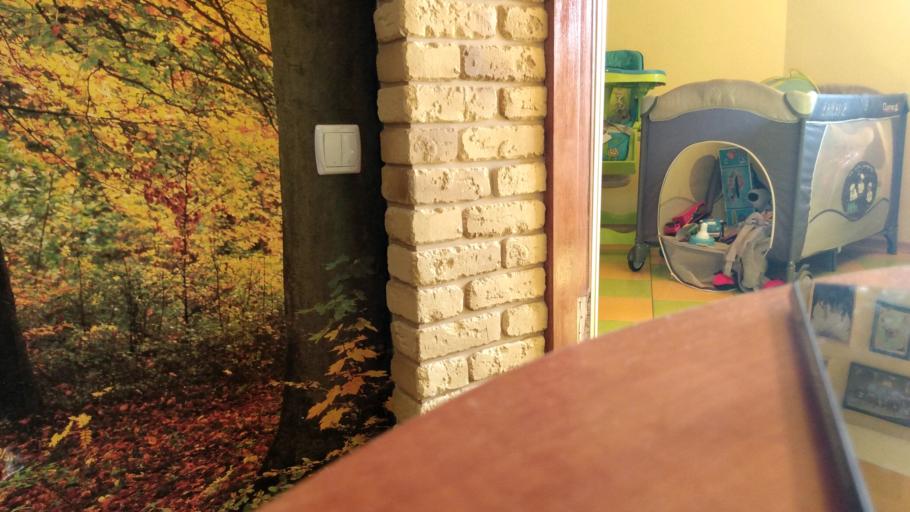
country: RU
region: Tverskaya
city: Vasil'yevskiy Mokh
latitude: 56.9998
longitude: 35.8797
